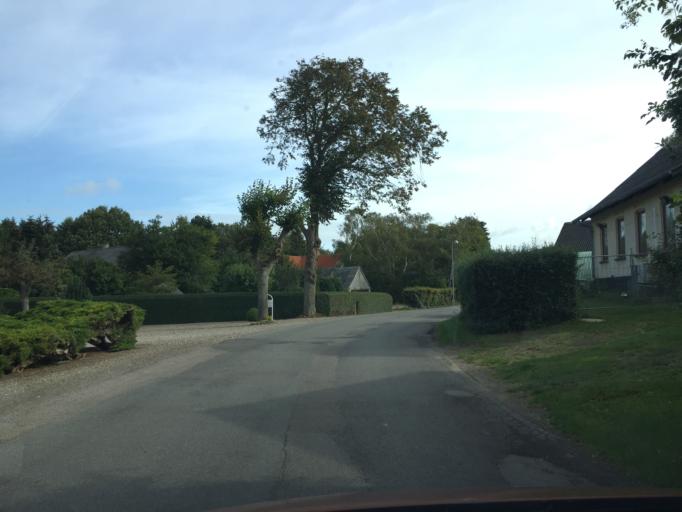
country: DK
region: Zealand
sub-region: Kalundborg Kommune
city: Kalundborg
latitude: 55.6310
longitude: 11.1582
